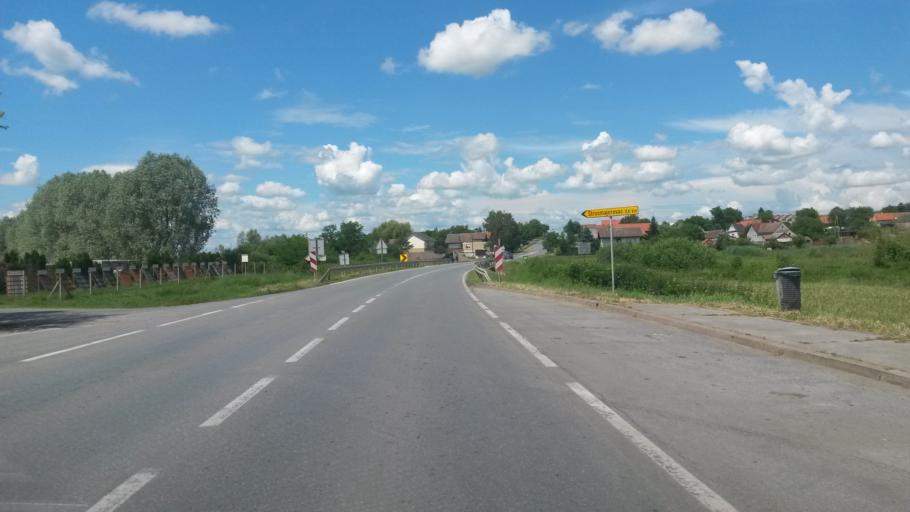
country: HR
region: Osjecko-Baranjska
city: Viskovci
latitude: 45.3425
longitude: 18.4211
